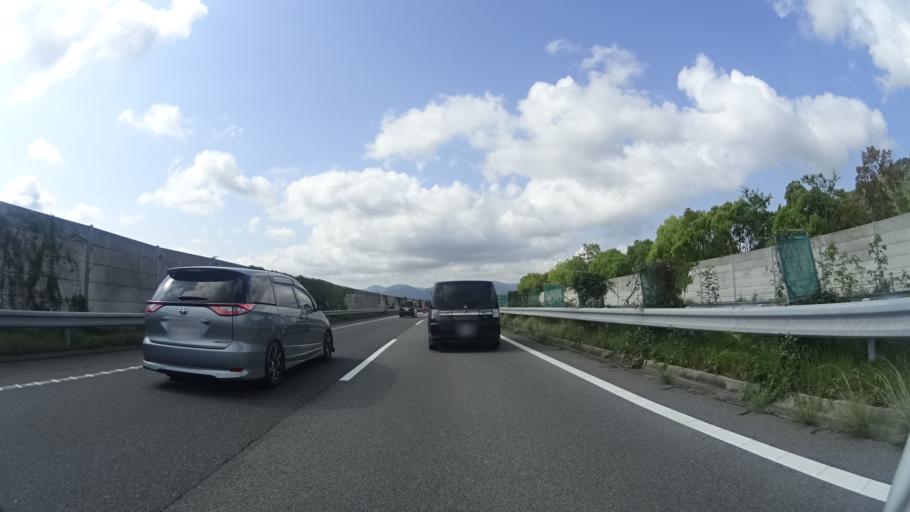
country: JP
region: Hyogo
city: Sumoto
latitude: 34.3629
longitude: 134.8580
